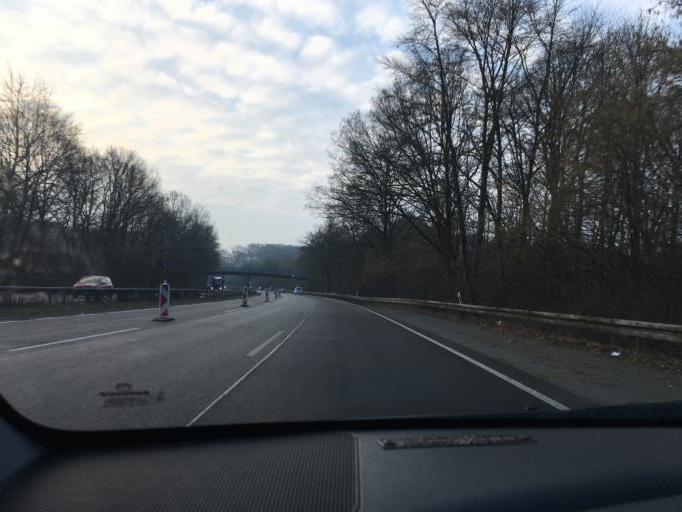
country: DE
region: North Rhine-Westphalia
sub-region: Regierungsbezirk Arnsberg
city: Dortmund
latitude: 51.4571
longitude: 7.4827
